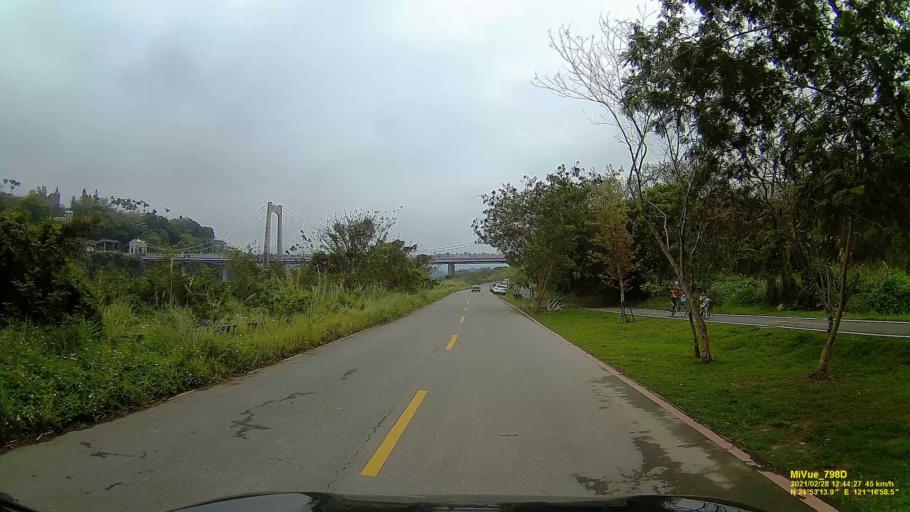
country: TW
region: Taiwan
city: Daxi
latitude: 24.8871
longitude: 121.2829
